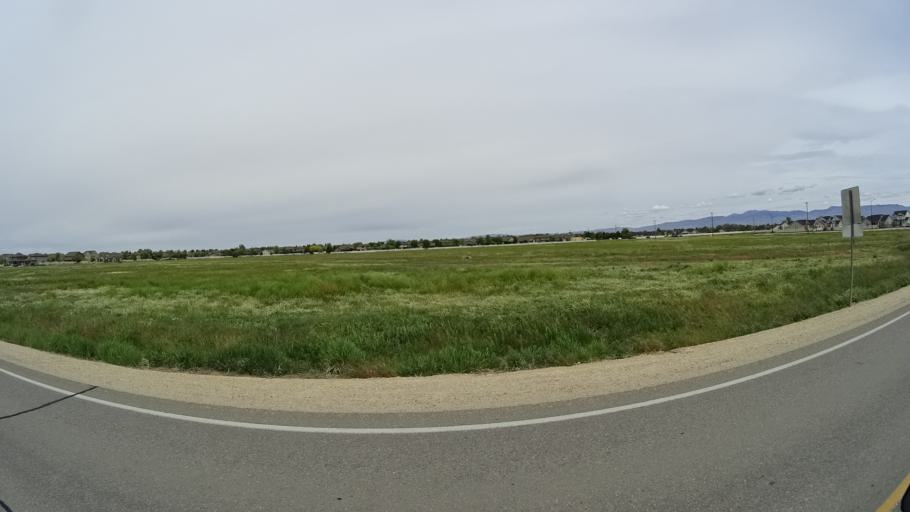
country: US
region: Idaho
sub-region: Ada County
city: Meridian
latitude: 43.5609
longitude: -116.3568
